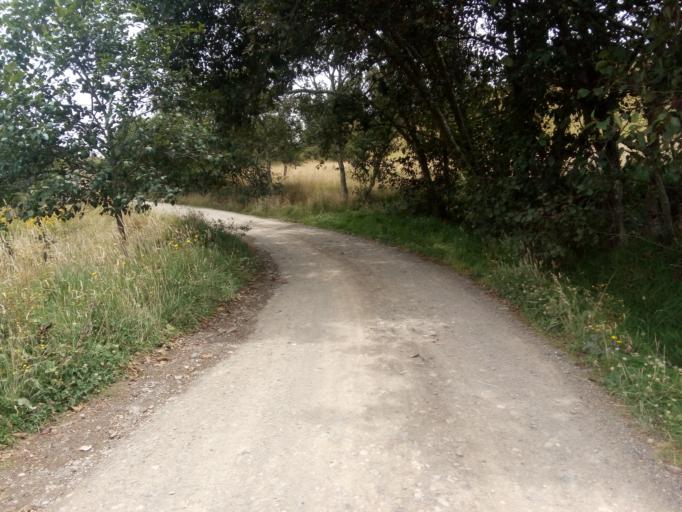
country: CO
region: Boyaca
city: Gameza
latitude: 5.8205
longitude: -72.8010
